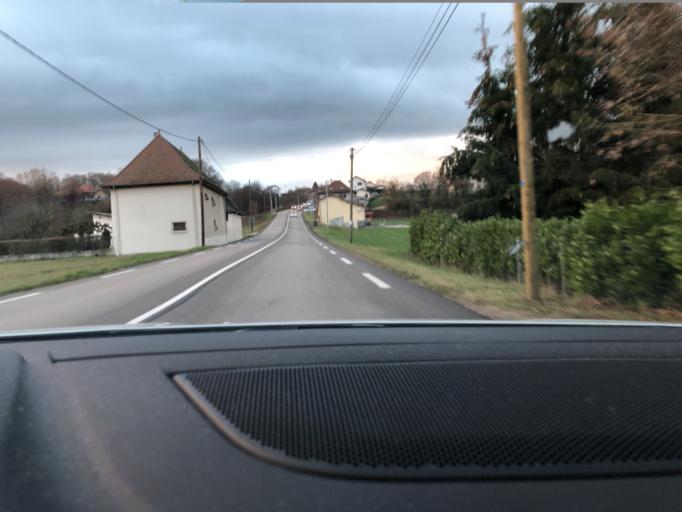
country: FR
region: Rhone-Alpes
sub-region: Departement de l'Isere
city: Saint-Andre-le-Gaz
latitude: 45.5355
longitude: 5.5383
